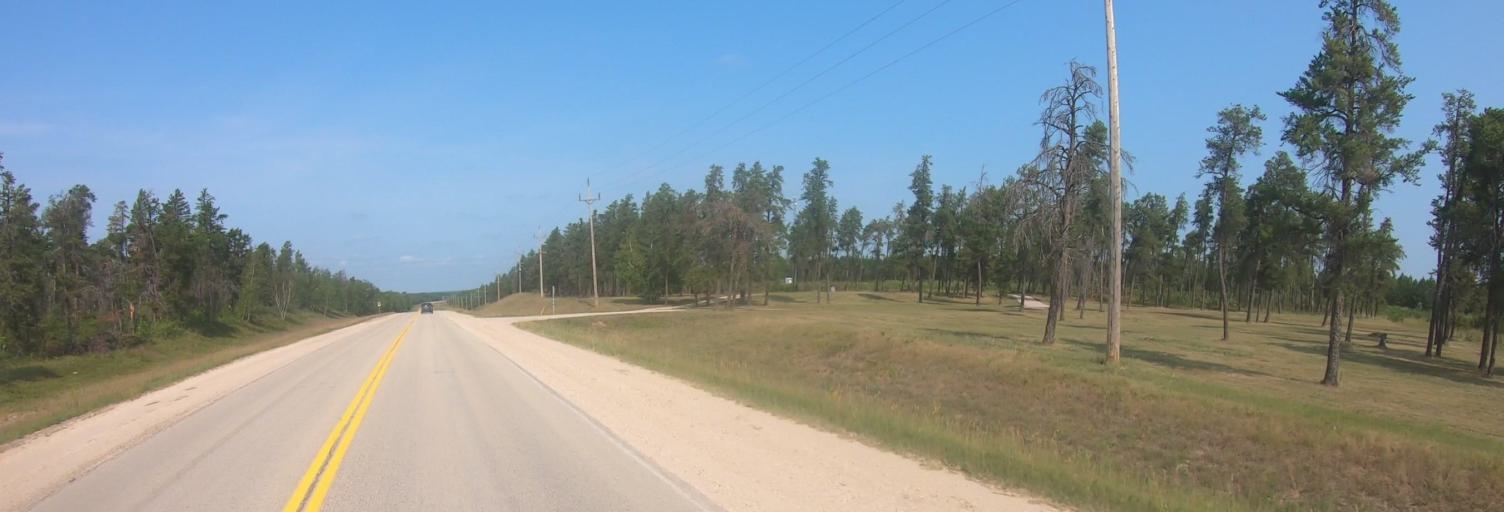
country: US
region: Minnesota
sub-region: Roseau County
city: Roseau
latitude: 49.1329
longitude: -96.0862
